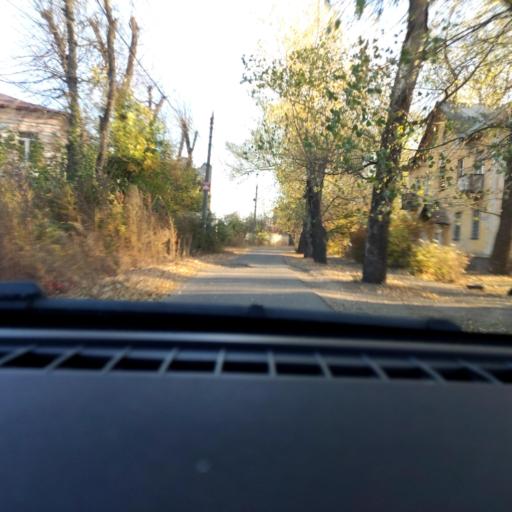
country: RU
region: Voronezj
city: Voronezh
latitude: 51.6645
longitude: 39.2726
